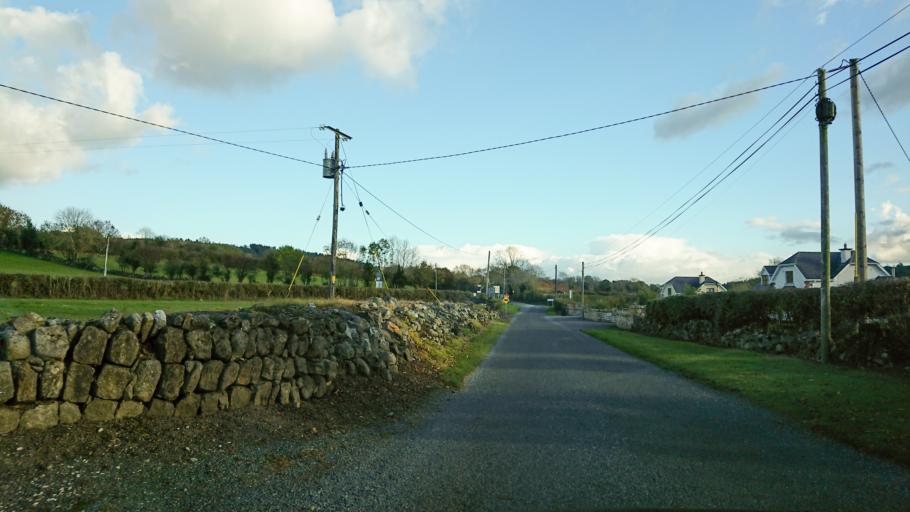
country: IE
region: Leinster
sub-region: Loch Garman
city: New Ross
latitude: 52.4718
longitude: -6.9019
